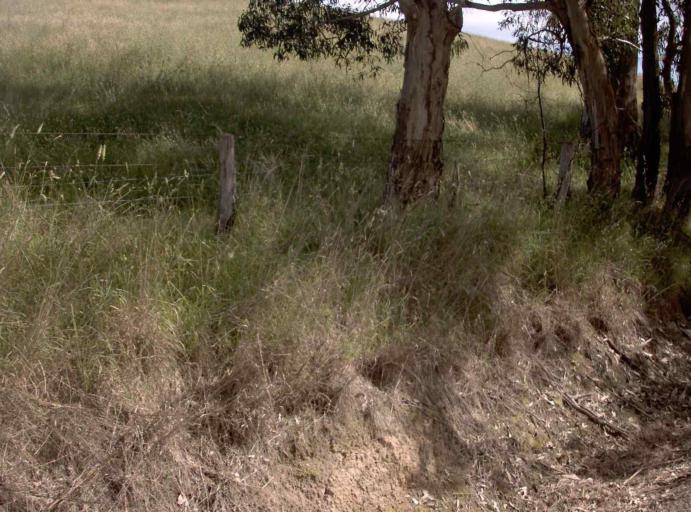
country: AU
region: Victoria
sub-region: East Gippsland
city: Lakes Entrance
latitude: -37.5210
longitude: 148.1399
